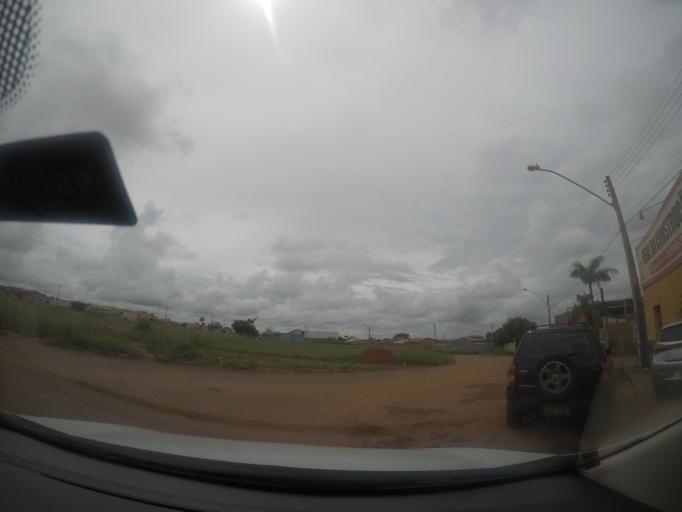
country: BR
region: Goias
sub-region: Trindade
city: Trindade
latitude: -16.6917
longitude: -49.3954
